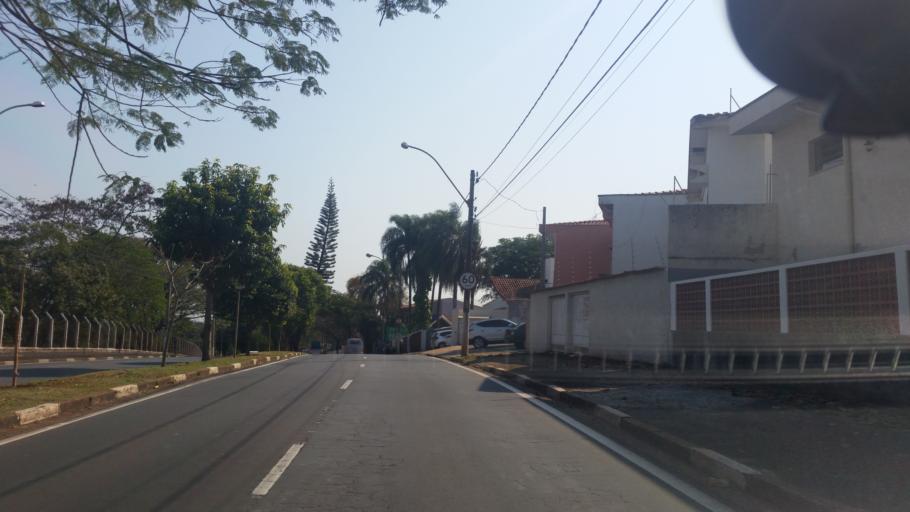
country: BR
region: Sao Paulo
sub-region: Campinas
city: Campinas
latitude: -22.8807
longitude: -47.0753
